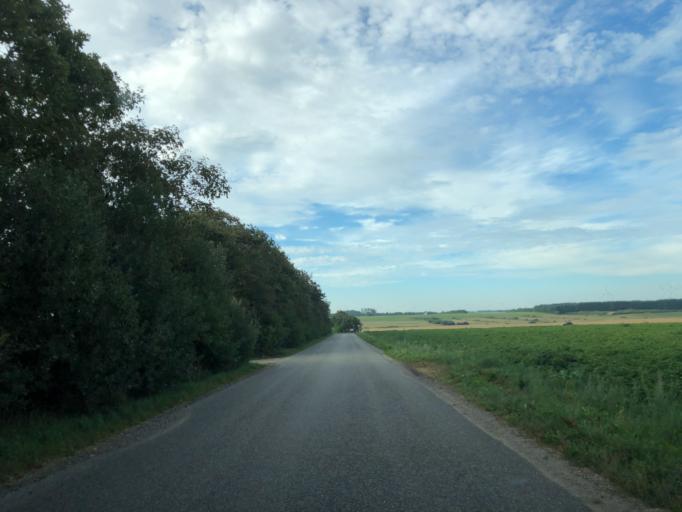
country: DK
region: Central Jutland
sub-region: Holstebro Kommune
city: Ulfborg
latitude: 56.1465
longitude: 8.4055
